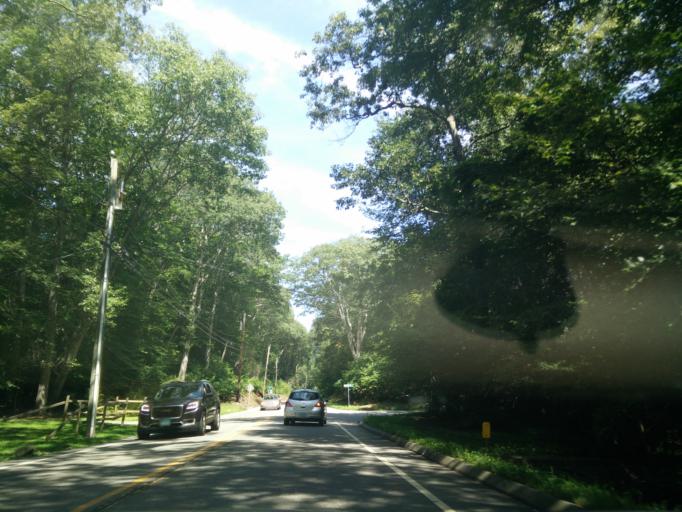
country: US
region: Connecticut
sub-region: Middlesex County
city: Clinton
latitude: 41.3260
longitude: -72.5491
